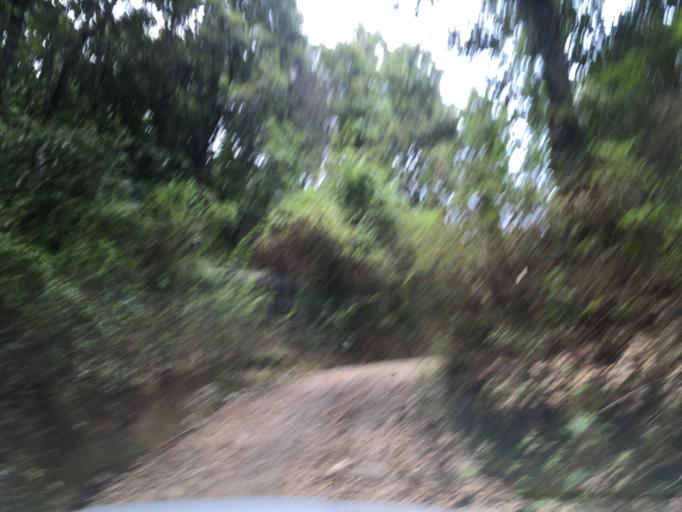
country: MX
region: Michoacan
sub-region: Zitacuaro
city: Macutzio
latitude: 19.5078
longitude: -100.3219
